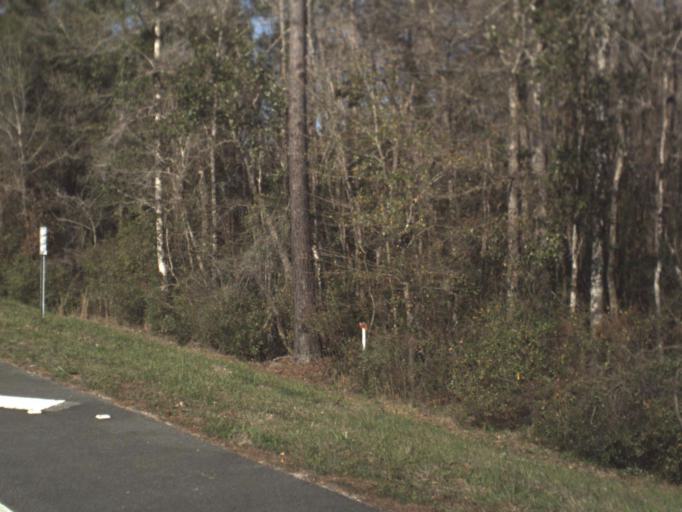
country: US
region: Florida
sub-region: Calhoun County
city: Blountstown
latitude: 30.3581
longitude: -85.2122
